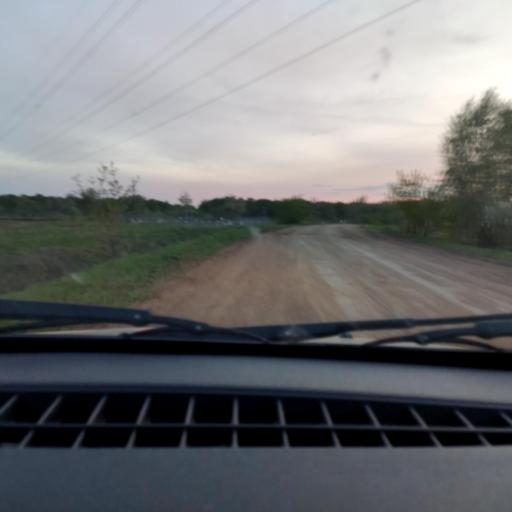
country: RU
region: Bashkortostan
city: Iglino
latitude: 54.8892
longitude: 56.3890
